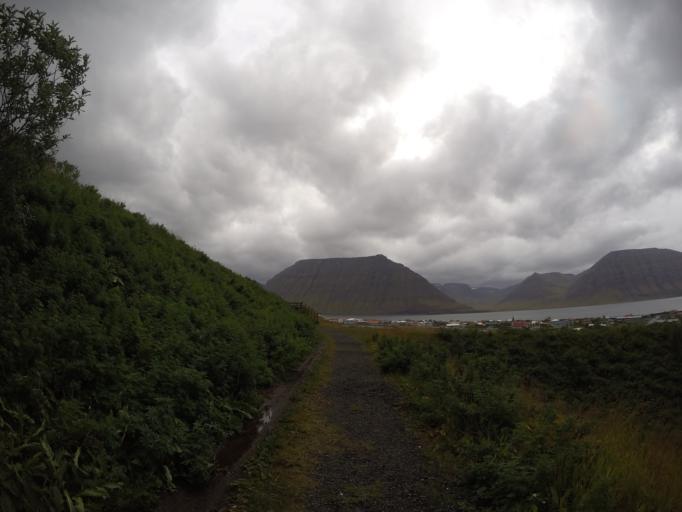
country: IS
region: Westfjords
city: Isafjoerdur
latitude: 66.0531
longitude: -23.5082
